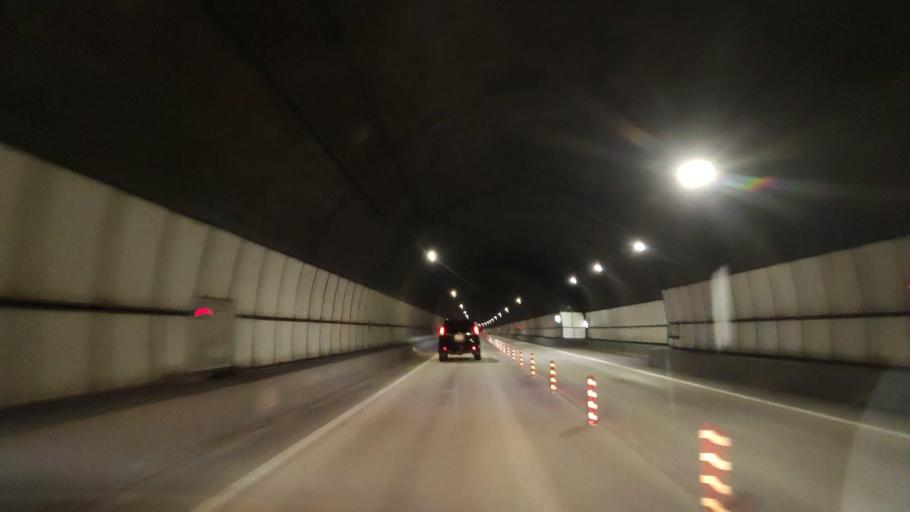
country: JP
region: Yamagata
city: Shinjo
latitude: 38.6838
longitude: 140.3162
